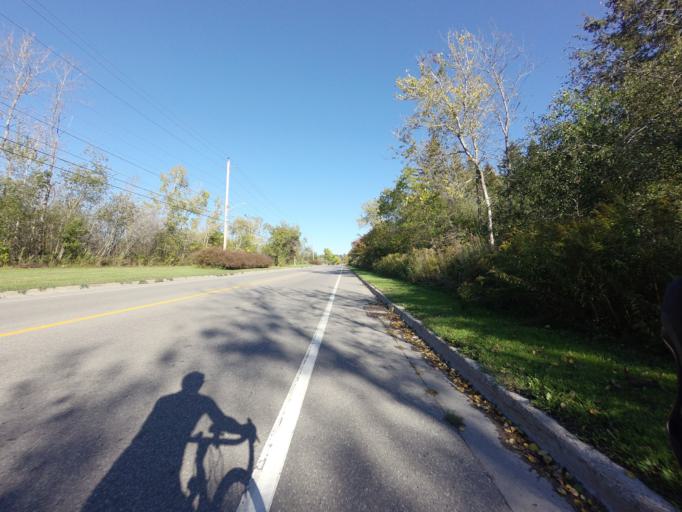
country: CA
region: Ontario
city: Oshawa
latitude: 43.8811
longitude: -78.8196
